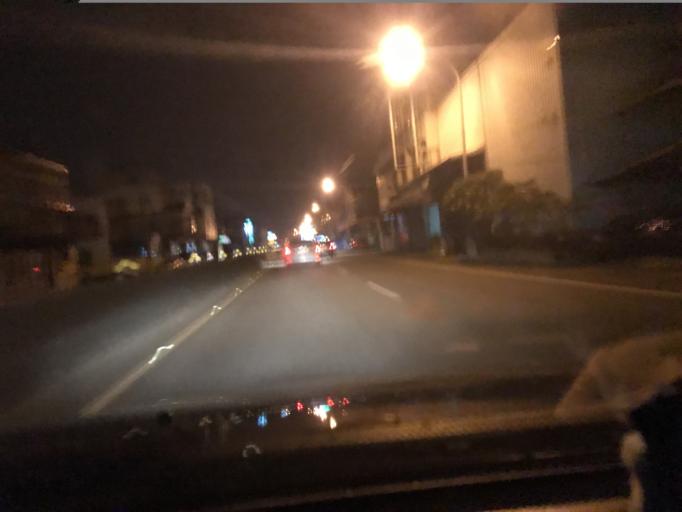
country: TW
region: Taiwan
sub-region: Hsinchu
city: Zhubei
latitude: 24.8018
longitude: 121.0516
